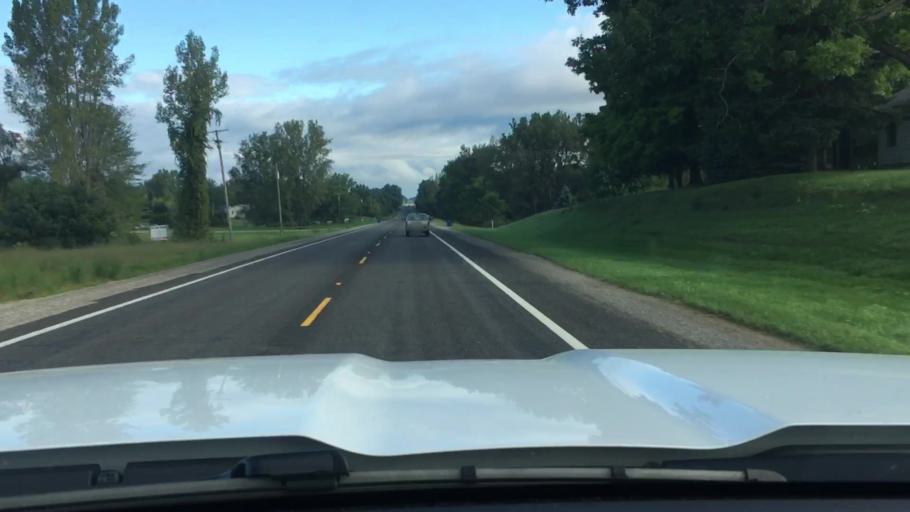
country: US
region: Michigan
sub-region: Tuscola County
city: Caro
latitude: 43.3549
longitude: -83.3827
